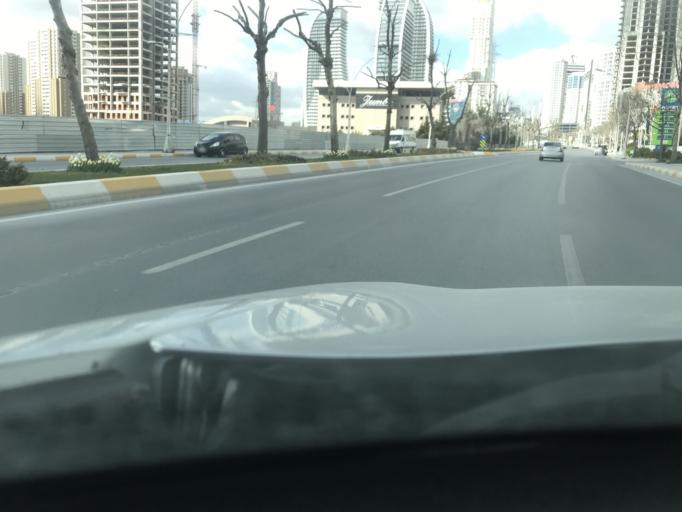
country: TR
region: Istanbul
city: Esenyurt
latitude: 41.0114
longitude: 28.6813
